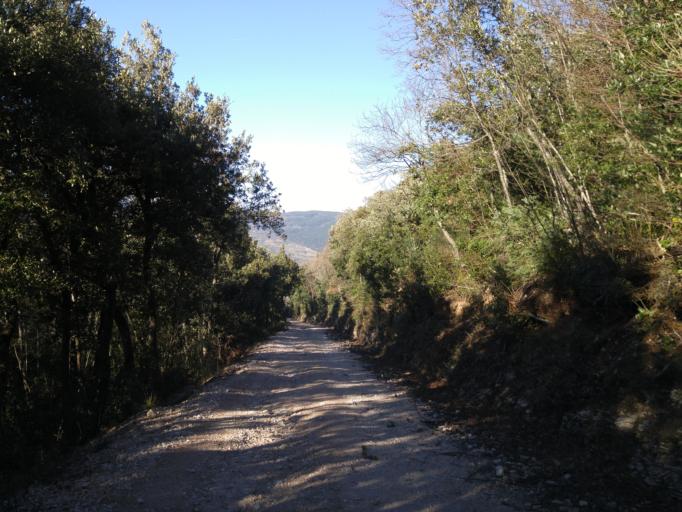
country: IT
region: The Marches
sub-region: Provincia di Pesaro e Urbino
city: Canavaccio
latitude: 43.6481
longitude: 12.7475
